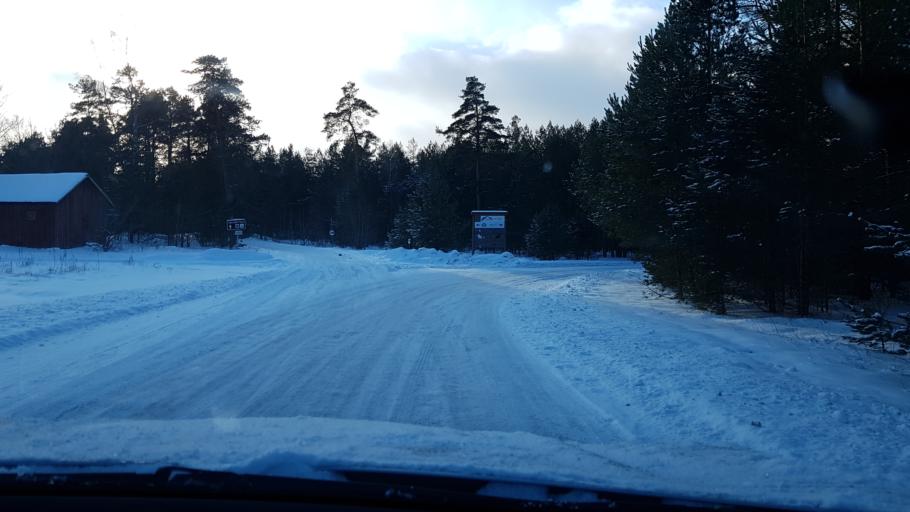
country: EE
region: Harju
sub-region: Nissi vald
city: Turba
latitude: 59.2250
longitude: 24.1620
